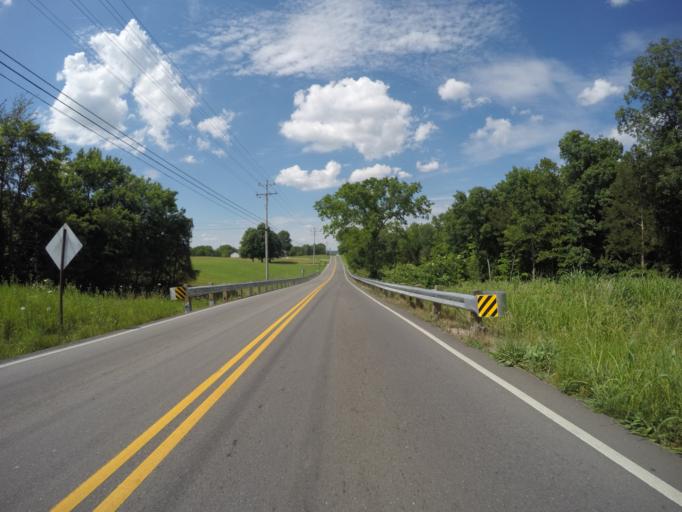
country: US
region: Tennessee
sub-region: Wilson County
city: Rural Hill
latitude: 36.1667
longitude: -86.4585
